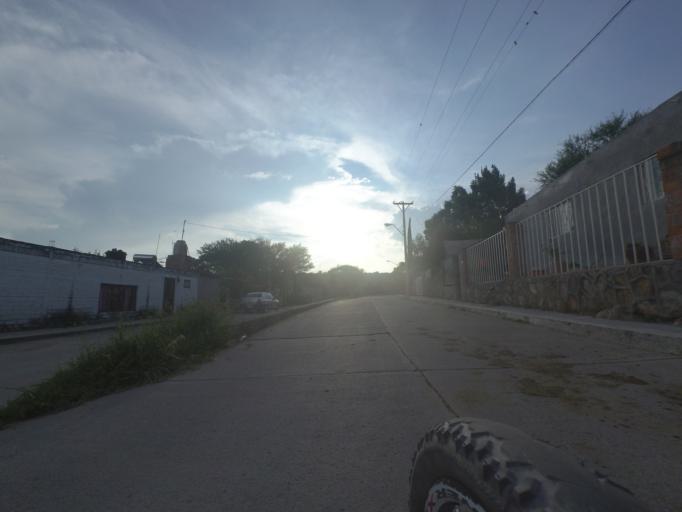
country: MX
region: Aguascalientes
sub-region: Aguascalientes
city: Los Canos
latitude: 21.7805
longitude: -102.3768
